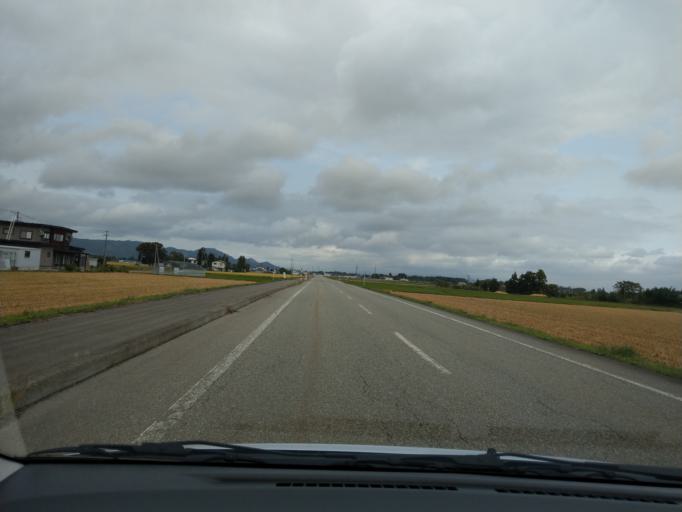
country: JP
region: Akita
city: Omagari
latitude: 39.3868
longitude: 140.4858
